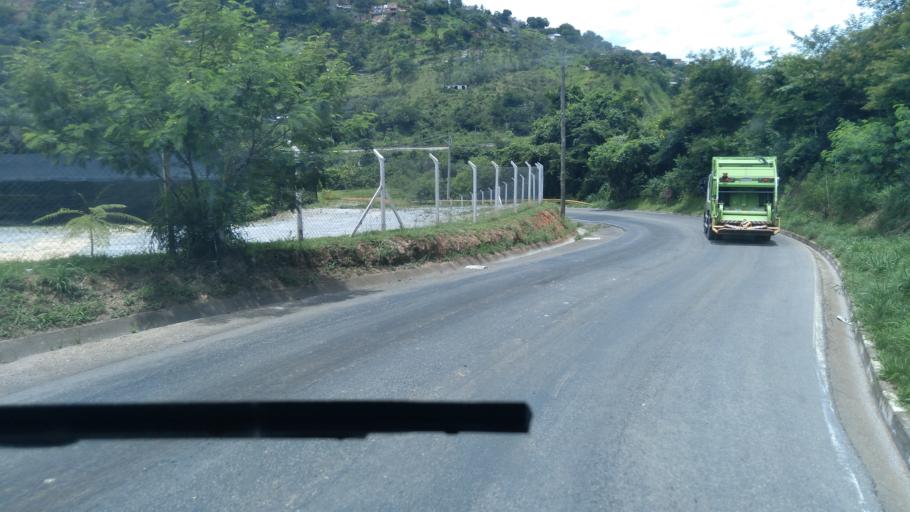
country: BR
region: Minas Gerais
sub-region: Santa Luzia
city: Santa Luzia
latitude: -19.8609
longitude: -43.8509
